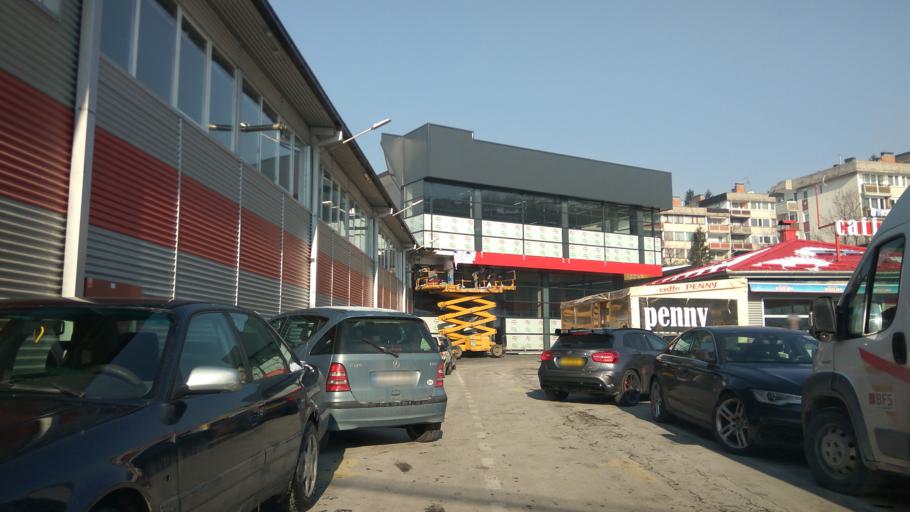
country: BA
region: Federation of Bosnia and Herzegovina
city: Kobilja Glava
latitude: 43.8655
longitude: 18.4027
